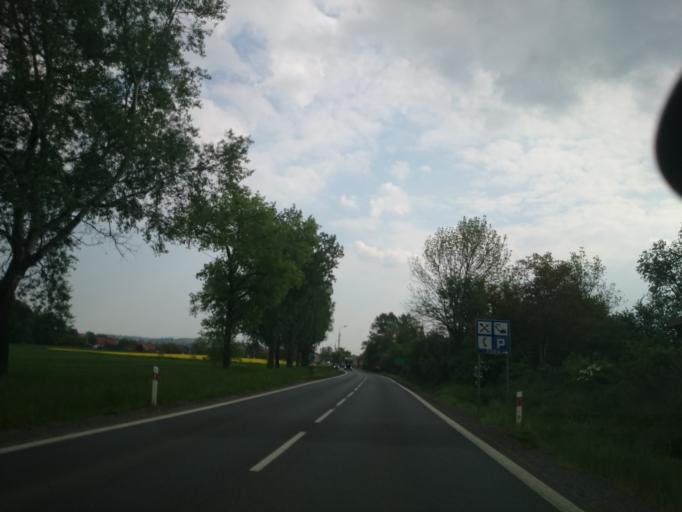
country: PL
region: Lower Silesian Voivodeship
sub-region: Powiat dzierzoniowski
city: Niemcza
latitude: 50.6893
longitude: 16.8203
